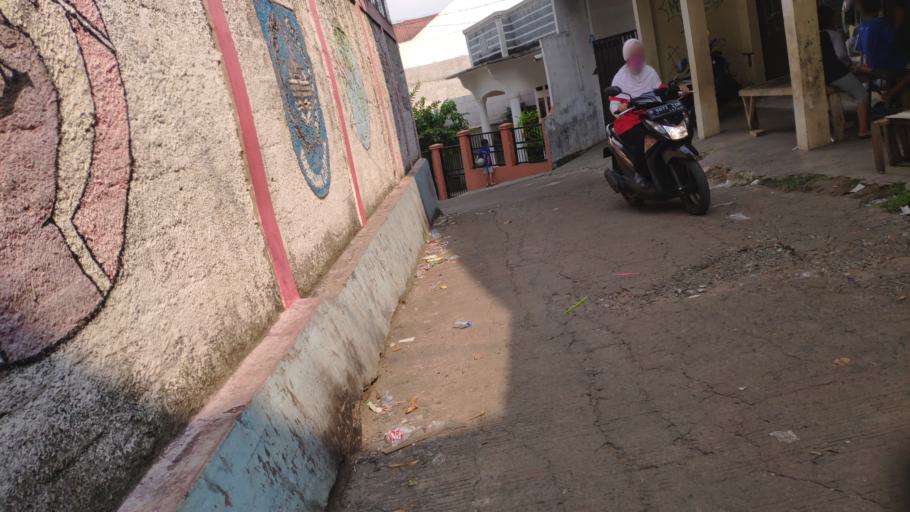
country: ID
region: West Java
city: Pamulang
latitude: -6.3427
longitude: 106.7904
